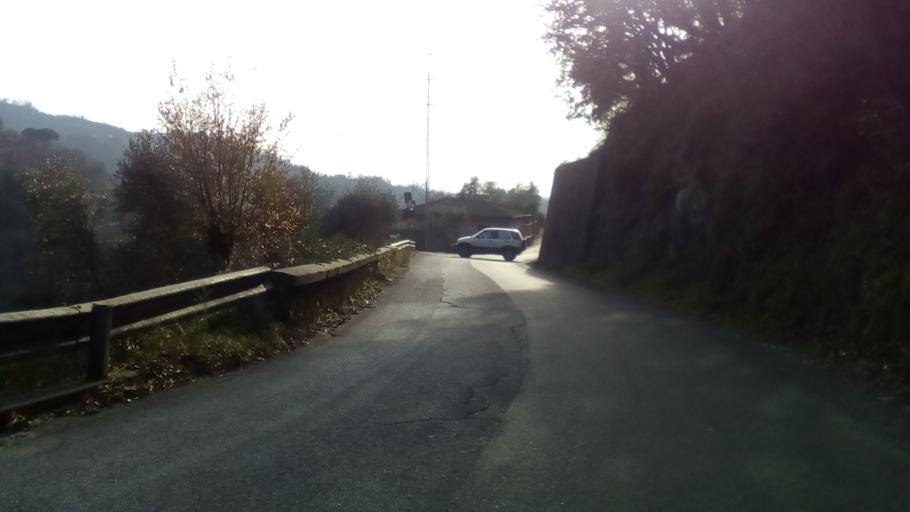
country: IT
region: Tuscany
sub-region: Provincia di Massa-Carrara
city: Carrara
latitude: 44.0839
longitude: 10.1094
